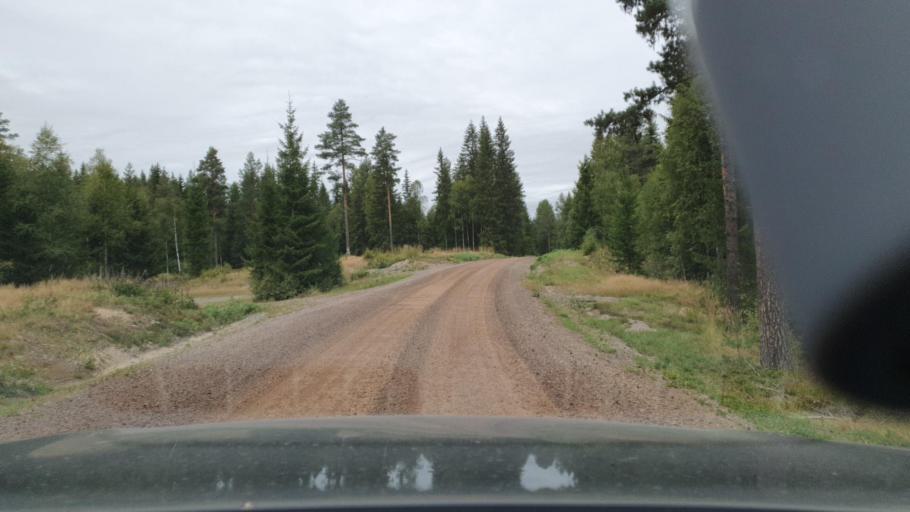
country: SE
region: Vaermland
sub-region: Eda Kommun
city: Charlottenberg
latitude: 60.0472
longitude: 12.5729
